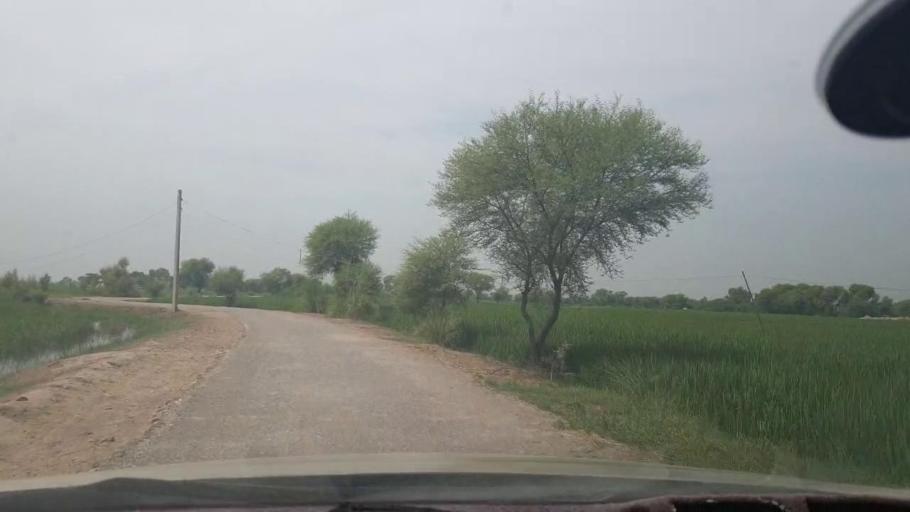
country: PK
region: Sindh
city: Jacobabad
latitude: 28.2430
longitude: 68.4269
